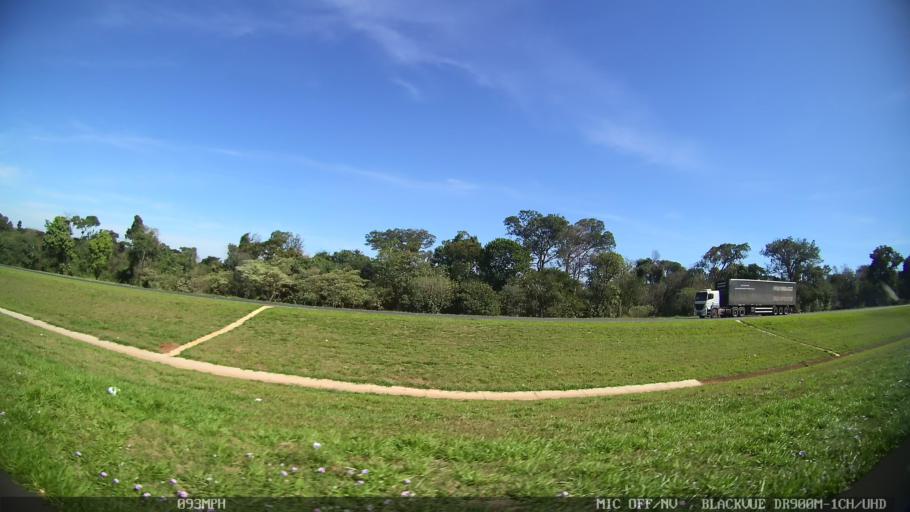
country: BR
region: Sao Paulo
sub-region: Santa Rita Do Passa Quatro
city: Santa Rita do Passa Quatro
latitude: -21.7201
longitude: -47.5887
